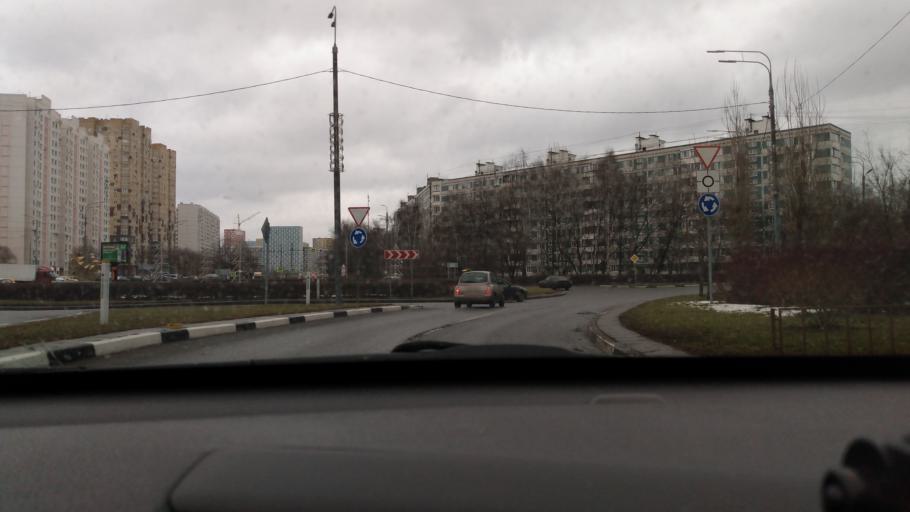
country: RU
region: Moscow
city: Yaroslavskiy
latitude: 55.9052
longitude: 37.7078
